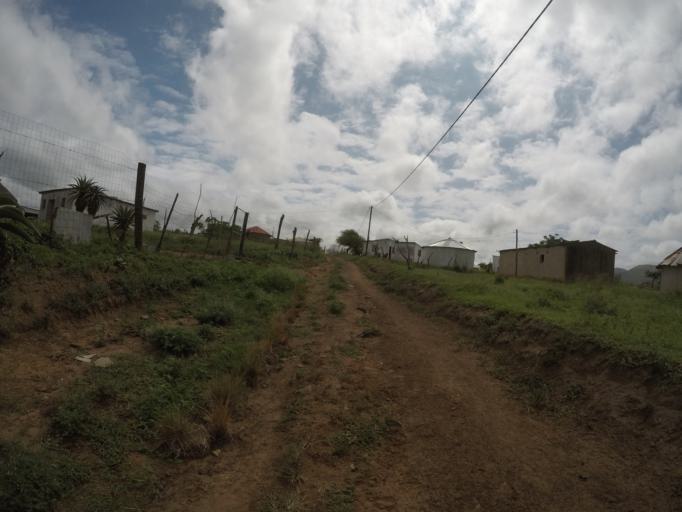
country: ZA
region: KwaZulu-Natal
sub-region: uThungulu District Municipality
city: Empangeni
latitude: -28.5830
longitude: 31.8494
